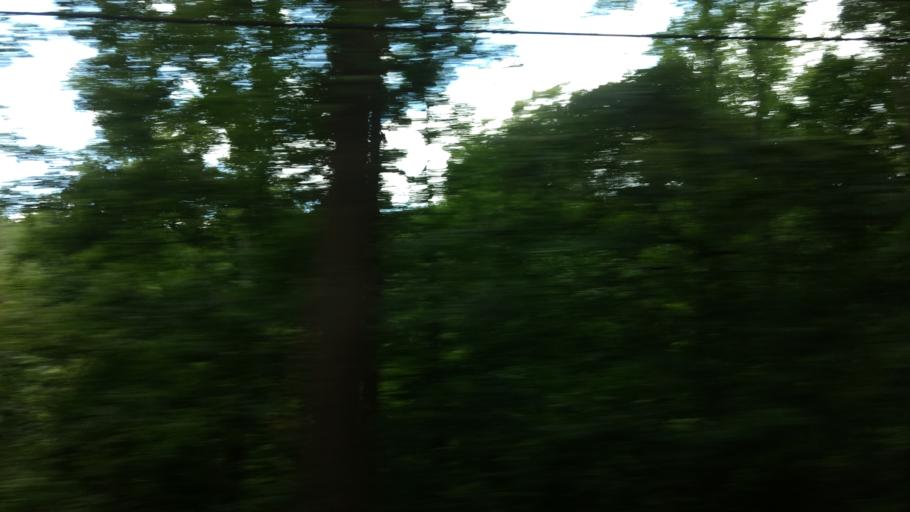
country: US
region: Pennsylvania
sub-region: Westmoreland County
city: Murrysville
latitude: 40.4756
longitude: -79.6759
